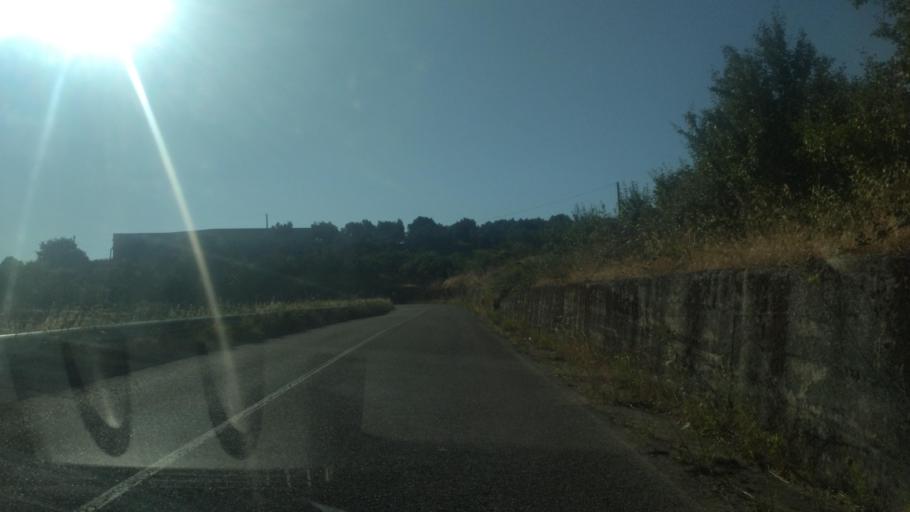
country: IT
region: Calabria
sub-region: Provincia di Catanzaro
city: Squillace
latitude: 38.7791
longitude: 16.5059
